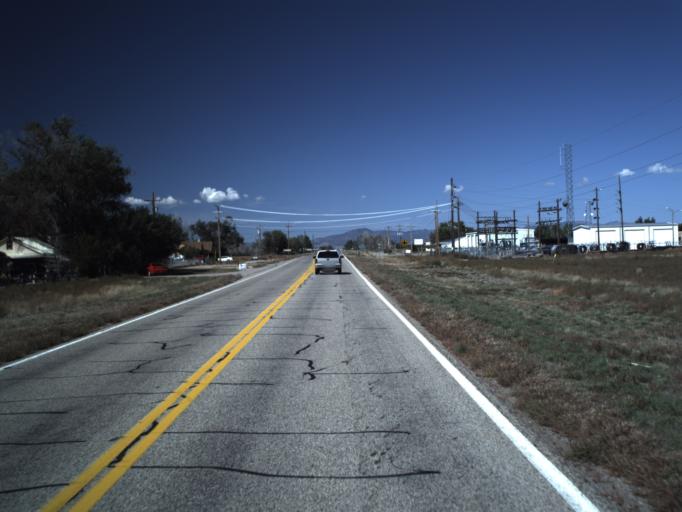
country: US
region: Utah
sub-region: Washington County
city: Enterprise
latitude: 37.7080
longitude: -113.6520
